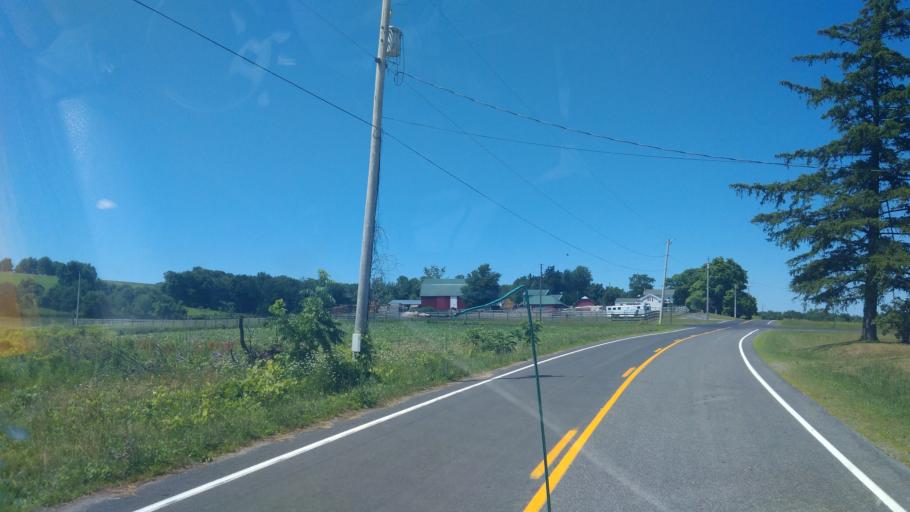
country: US
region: New York
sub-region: Wayne County
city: Lyons
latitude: 43.1346
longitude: -76.9597
